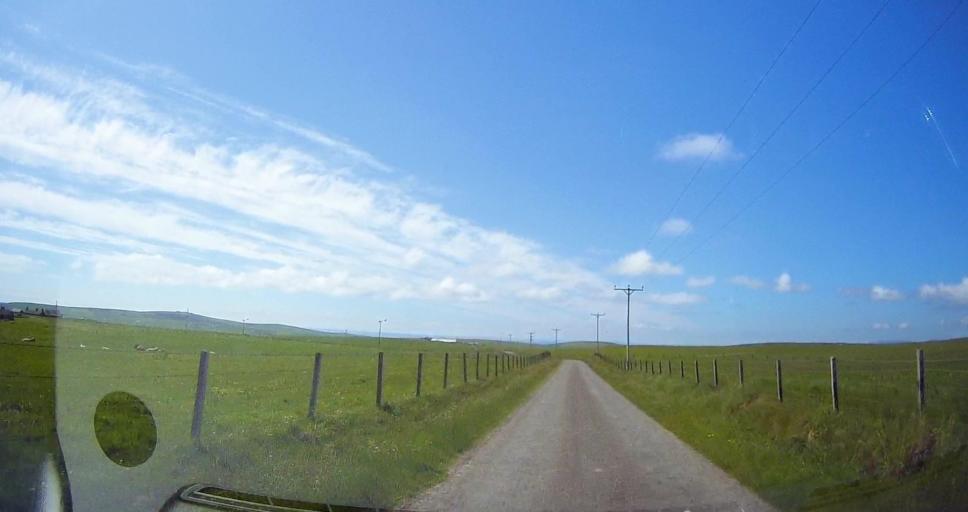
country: GB
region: Scotland
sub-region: Orkney Islands
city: Kirkwall
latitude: 58.8130
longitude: -2.9233
